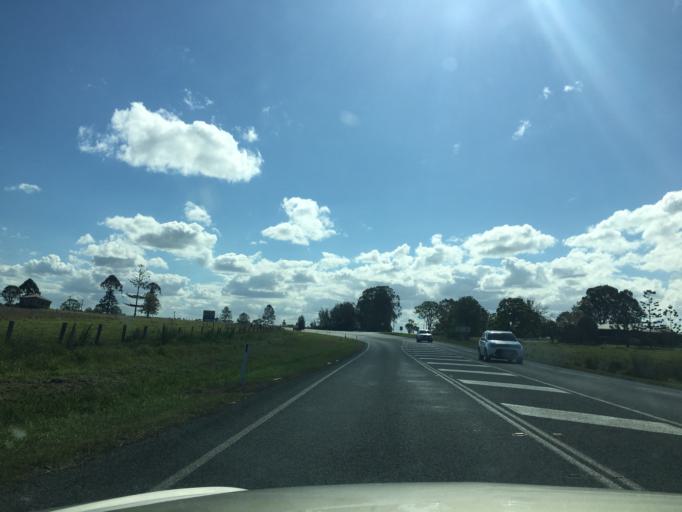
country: AU
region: Queensland
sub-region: Logan
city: Waterford West
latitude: -27.7080
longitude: 153.1360
